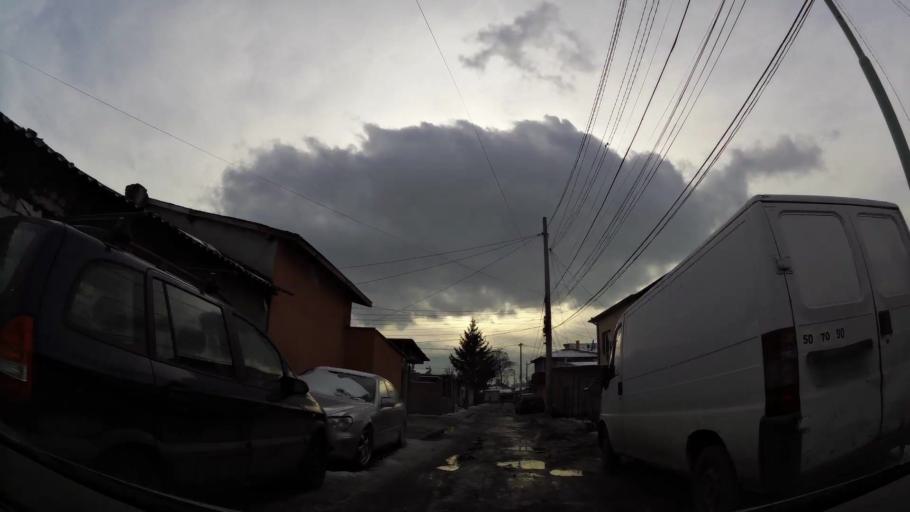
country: BG
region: Sofia-Capital
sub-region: Stolichna Obshtina
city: Sofia
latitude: 42.6871
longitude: 23.3852
